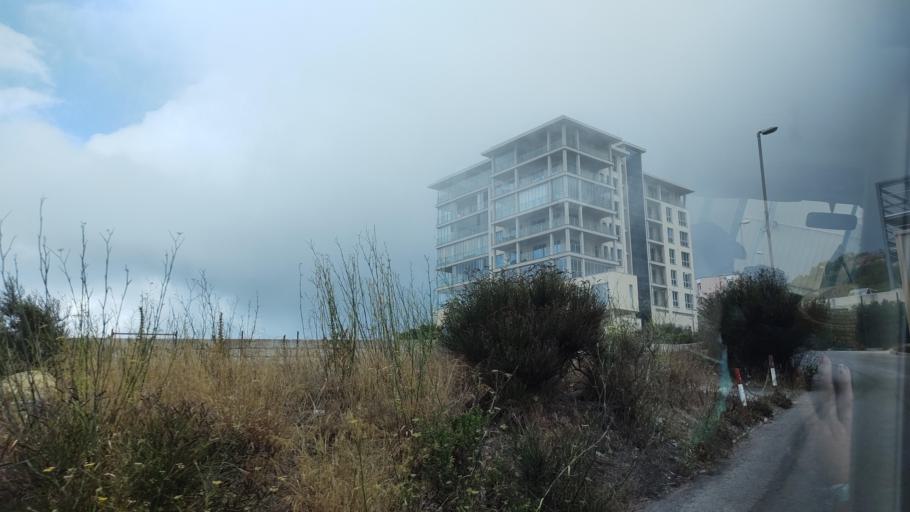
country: GI
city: Gibraltar
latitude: 36.1187
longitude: -5.3454
